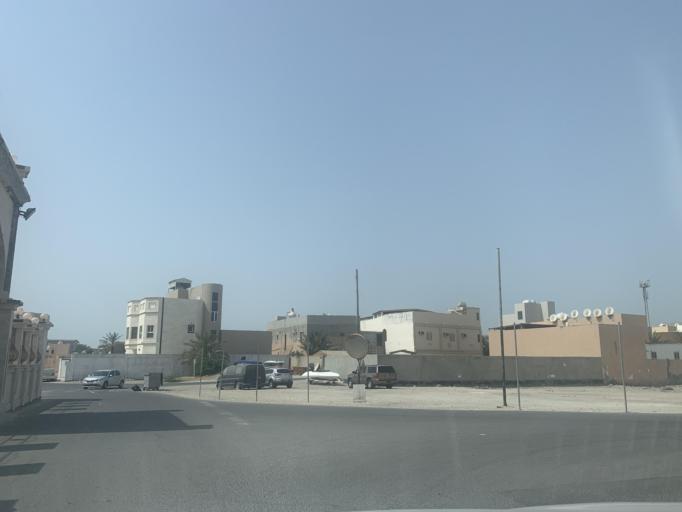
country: BH
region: Manama
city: Jidd Hafs
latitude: 26.2191
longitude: 50.4676
